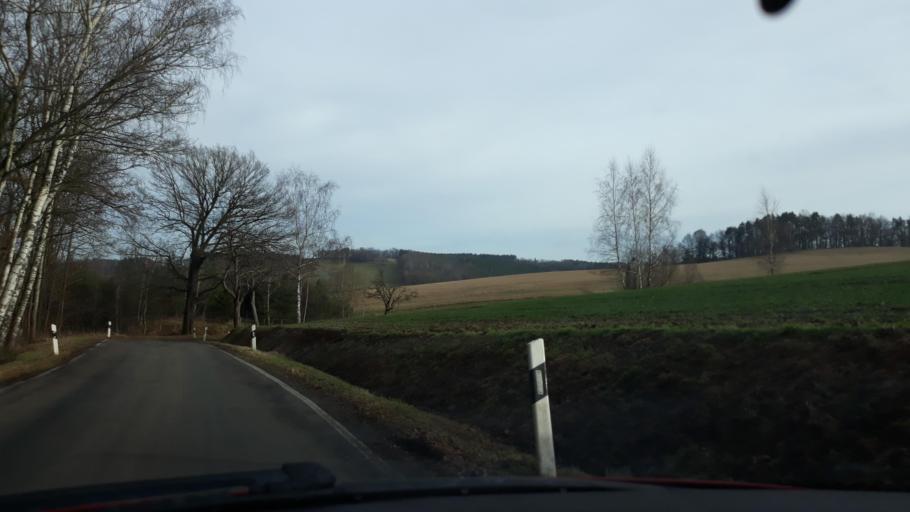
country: DE
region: Saxony
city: Kirchberg
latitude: 50.6433
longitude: 12.5070
